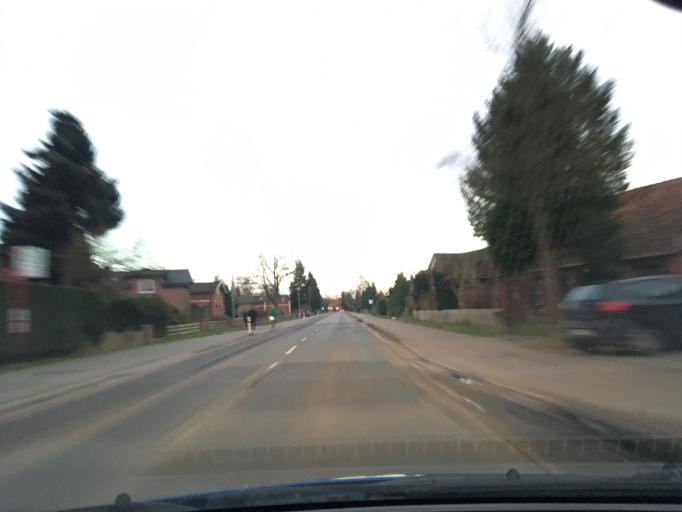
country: DE
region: Lower Saxony
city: Tespe
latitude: 53.3897
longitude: 10.4149
